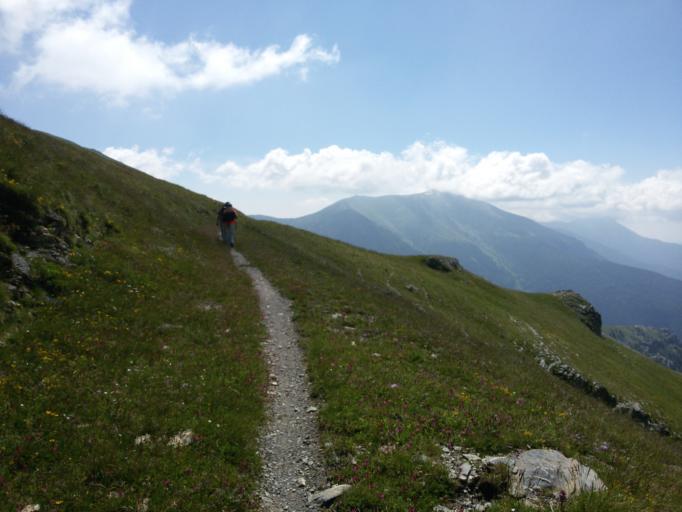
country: IT
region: Piedmont
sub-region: Provincia di Cuneo
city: Limone Piemonte
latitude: 44.1491
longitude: 7.6109
